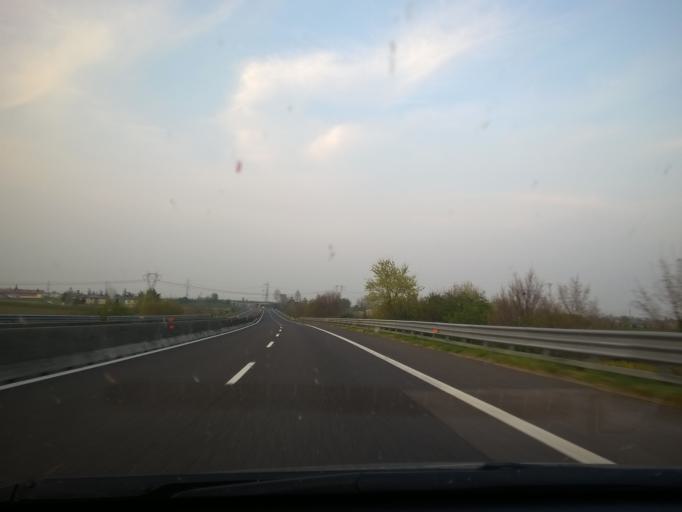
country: IT
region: Veneto
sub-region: Provincia di Padova
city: Ponte San Nicolo
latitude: 45.3551
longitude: 11.9389
